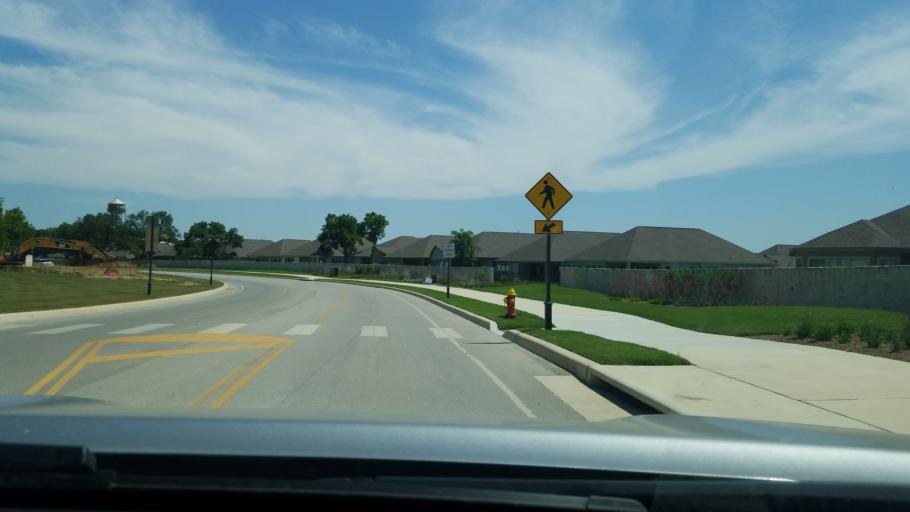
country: US
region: Texas
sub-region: Kendall County
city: Boerne
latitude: 29.8039
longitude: -98.6936
